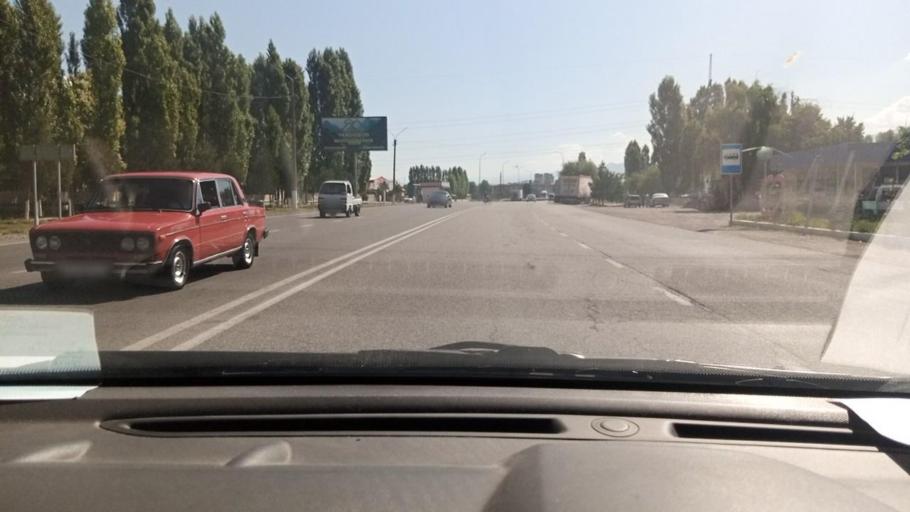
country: UZ
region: Toshkent
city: Angren
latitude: 40.9915
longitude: 70.0440
